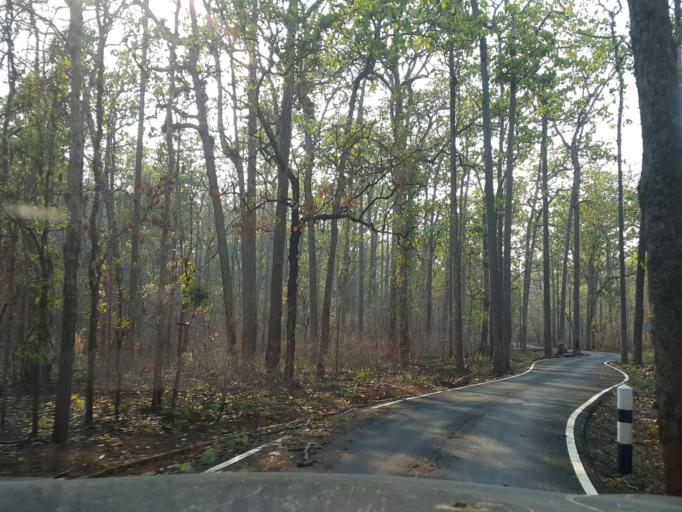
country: TH
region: Lamphun
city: Li
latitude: 17.6435
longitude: 98.8809
